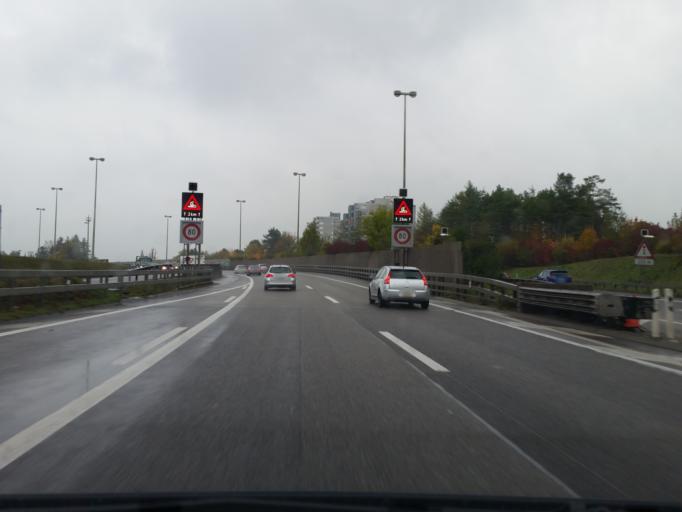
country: CH
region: Zurich
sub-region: Bezirk Zuerich
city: Zuerich (Kreis 12) / Auzelg
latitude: 47.4209
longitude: 8.5745
